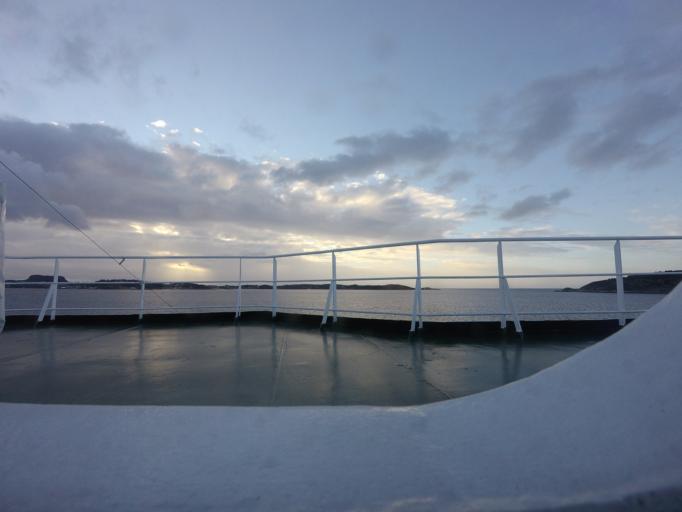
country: NO
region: More og Romsdal
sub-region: Kristiansund
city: Kristiansund
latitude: 63.1041
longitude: 7.7107
